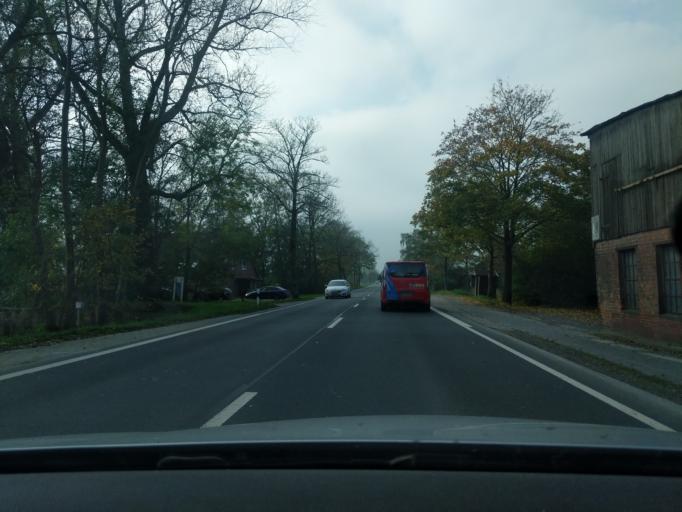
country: DE
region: Lower Saxony
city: Osterbruch
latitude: 53.8203
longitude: 8.9410
